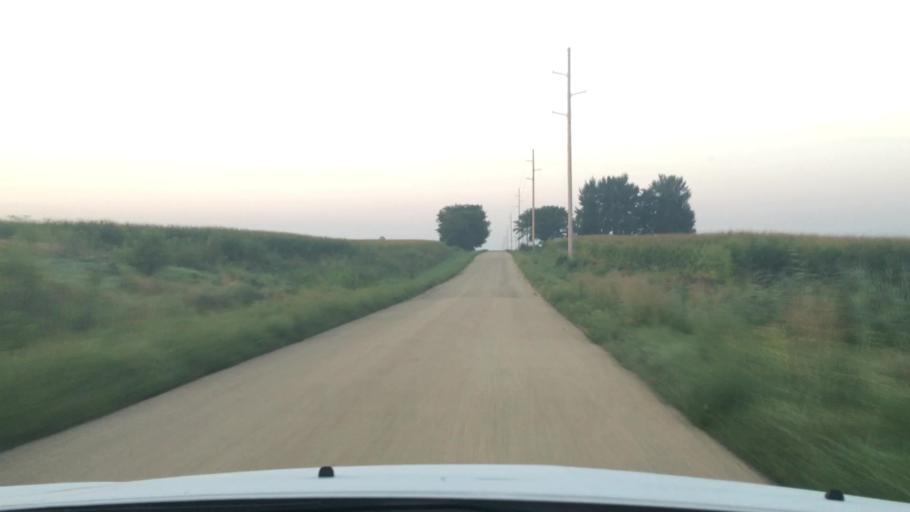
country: US
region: Illinois
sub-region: Ogle County
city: Rochelle
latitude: 41.8648
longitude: -89.0007
